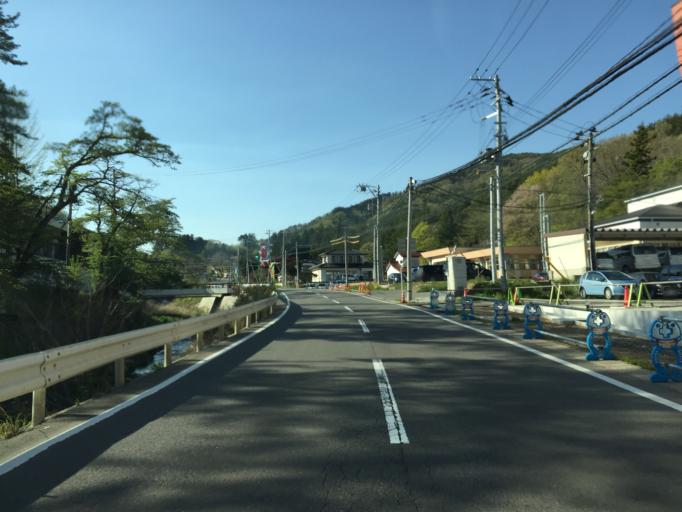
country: JP
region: Fukushima
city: Funehikimachi-funehiki
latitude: 37.5032
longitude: 140.7639
